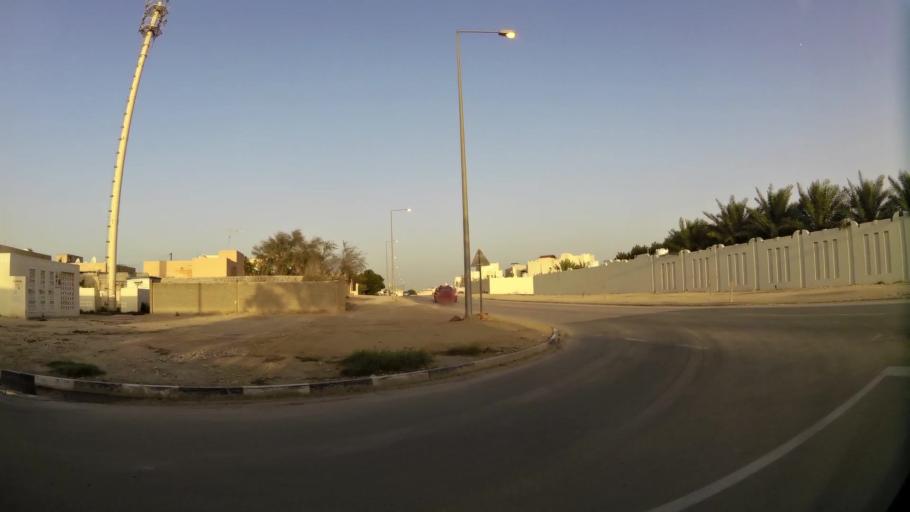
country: QA
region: Baladiyat ar Rayyan
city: Ar Rayyan
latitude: 25.3135
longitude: 51.4534
